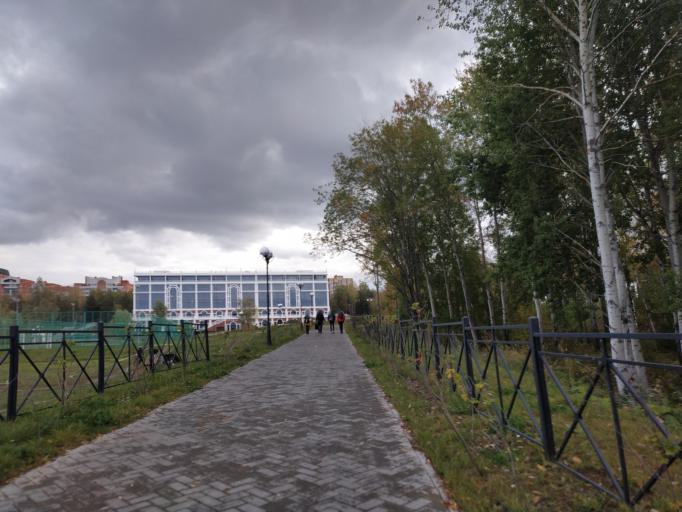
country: RU
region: Chuvashia
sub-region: Cheboksarskiy Rayon
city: Cheboksary
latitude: 56.1478
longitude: 47.2113
